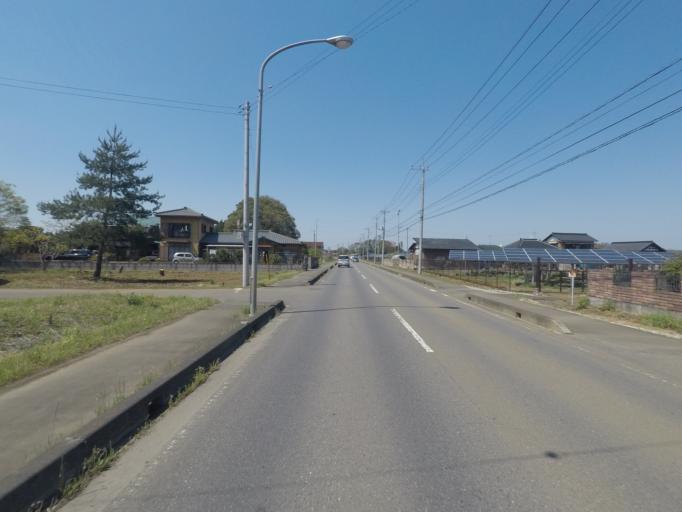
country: JP
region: Ibaraki
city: Ushiku
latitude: 35.9673
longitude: 140.1002
